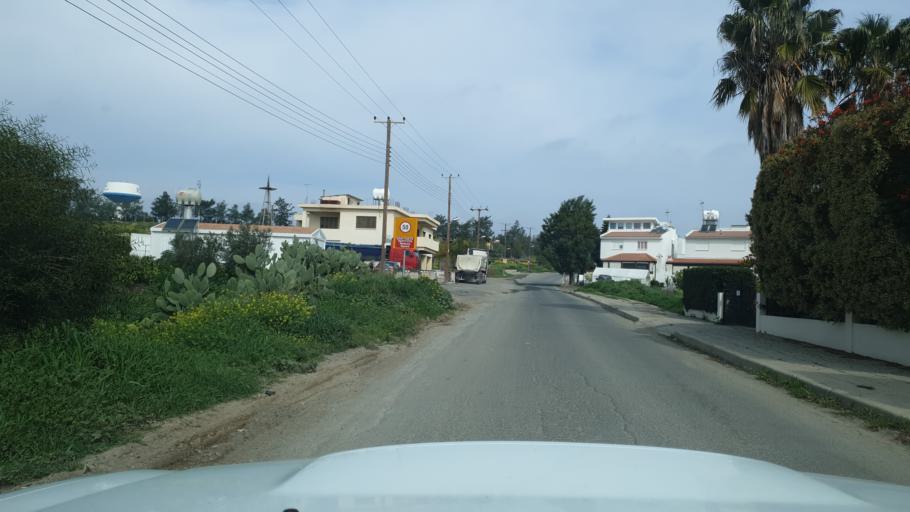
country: CY
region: Lefkosia
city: Tseri
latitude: 35.1191
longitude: 33.3447
